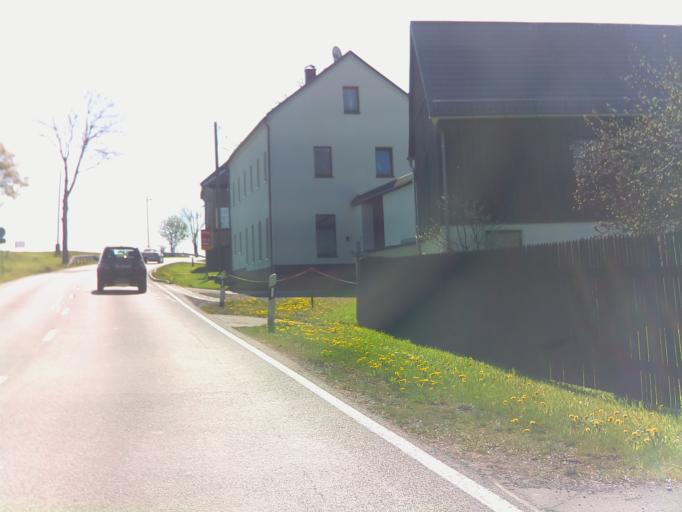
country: DE
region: Saxony
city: Mehltheuer
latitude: 50.5490
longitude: 12.0149
